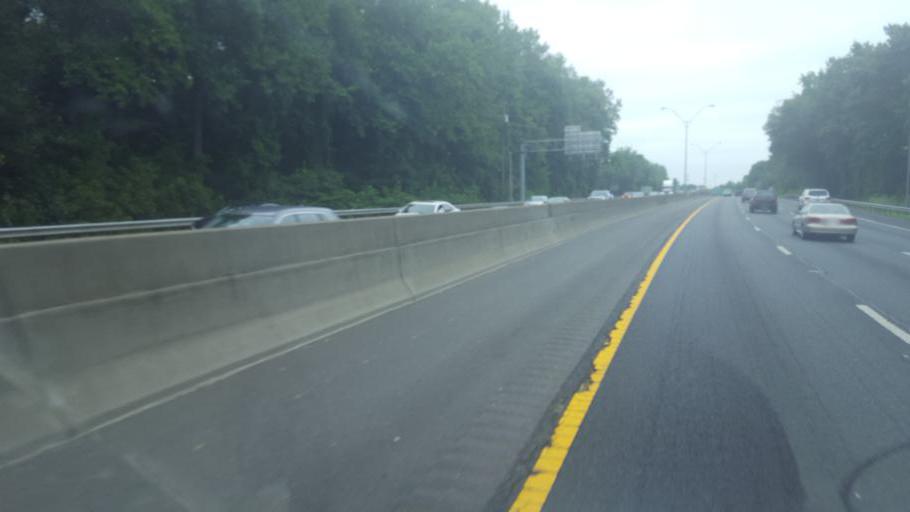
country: US
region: North Carolina
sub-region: Mecklenburg County
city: Charlotte
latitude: 35.2040
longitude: -80.8795
